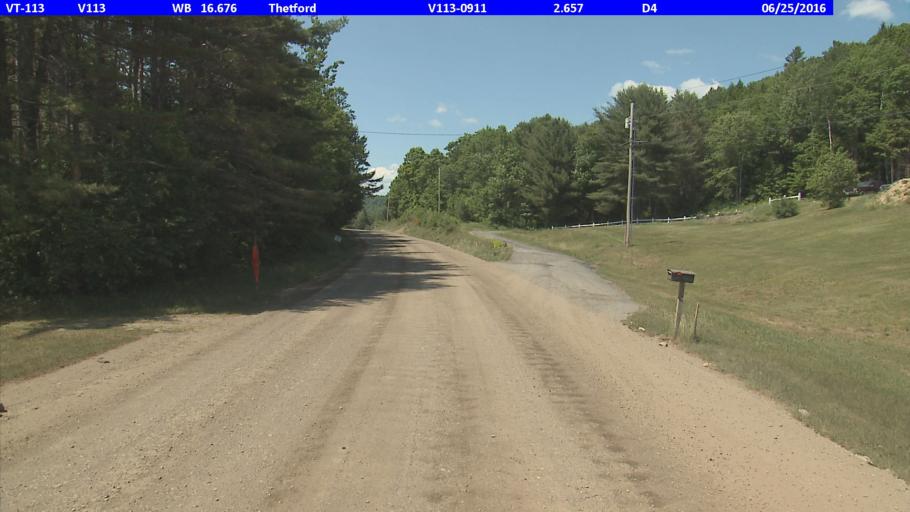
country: US
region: New Hampshire
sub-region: Grafton County
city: Lyme
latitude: 43.8606
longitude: -72.2600
